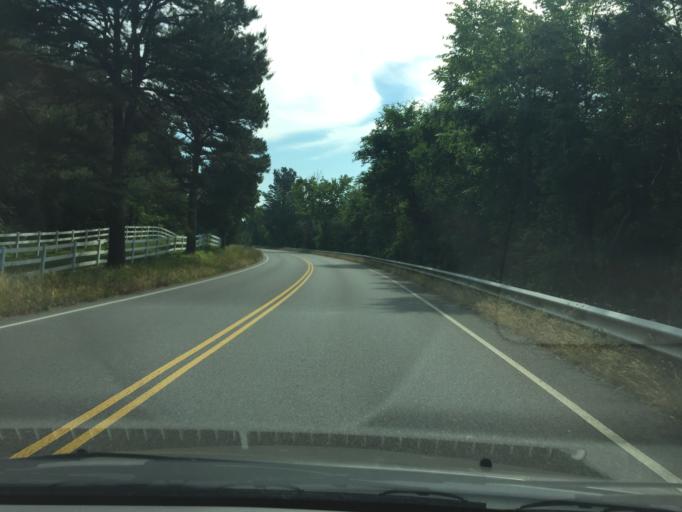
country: US
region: Tennessee
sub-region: Hamilton County
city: Collegedale
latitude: 35.1076
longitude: -84.9982
